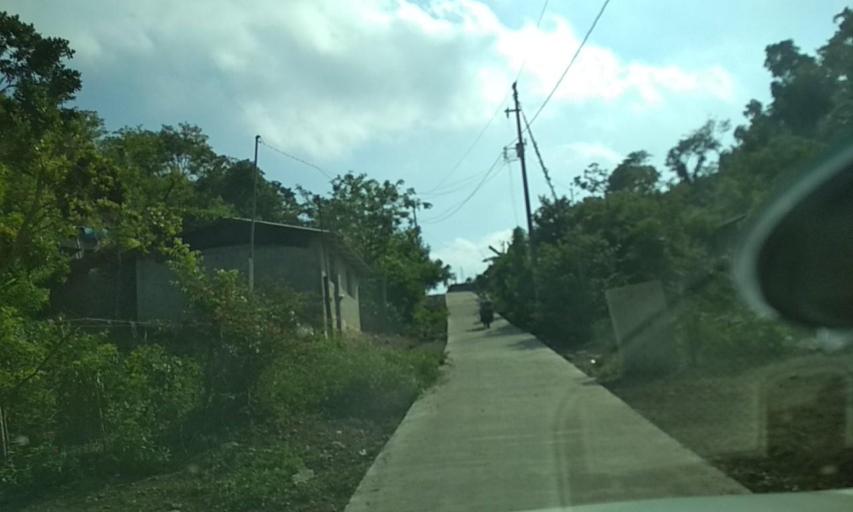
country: MX
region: Veracruz
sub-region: Cazones de Herrera
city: Rancho Nuevo
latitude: 20.6180
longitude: -97.2211
